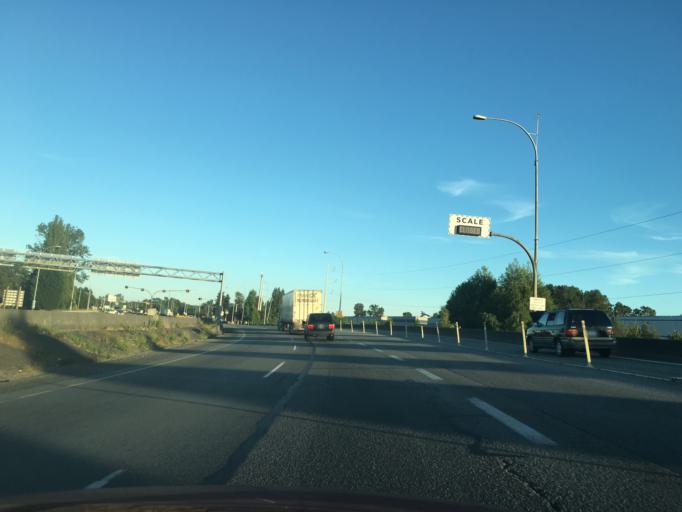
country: CA
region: British Columbia
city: Ladner
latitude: 49.1312
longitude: -123.0868
